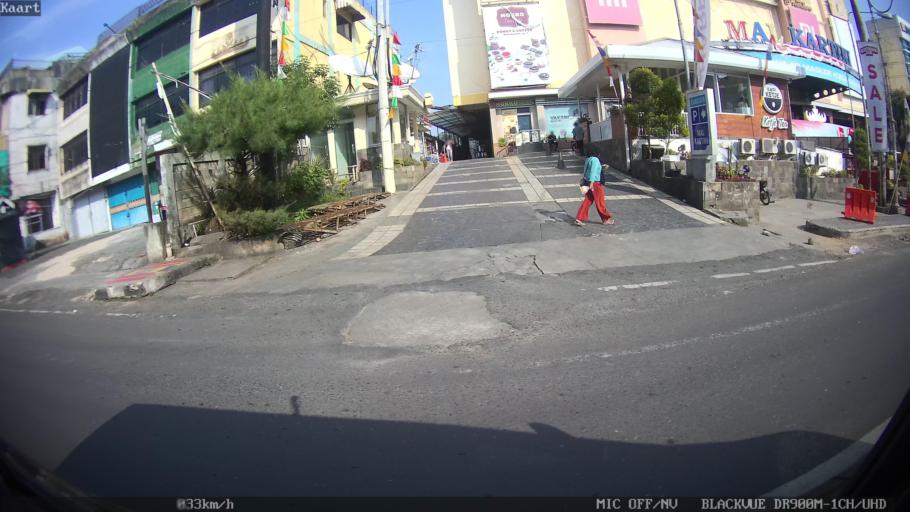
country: ID
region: Lampung
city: Bandarlampung
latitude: -5.4175
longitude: 105.2537
